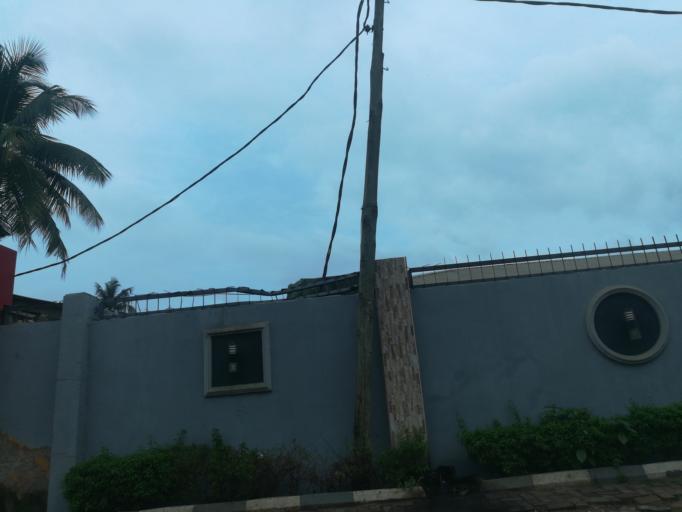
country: NG
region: Lagos
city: Oshodi
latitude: 6.5735
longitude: 3.3583
